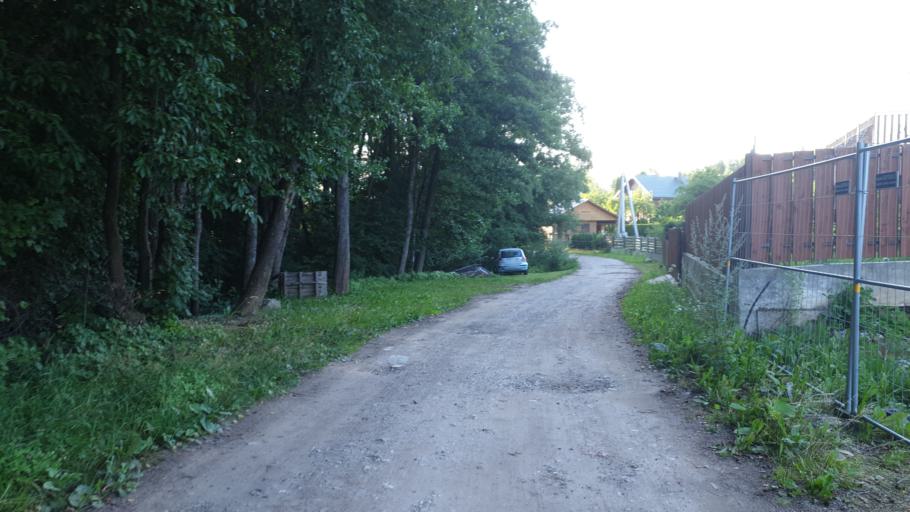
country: LT
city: Grigiskes
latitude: 54.7623
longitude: 25.0289
